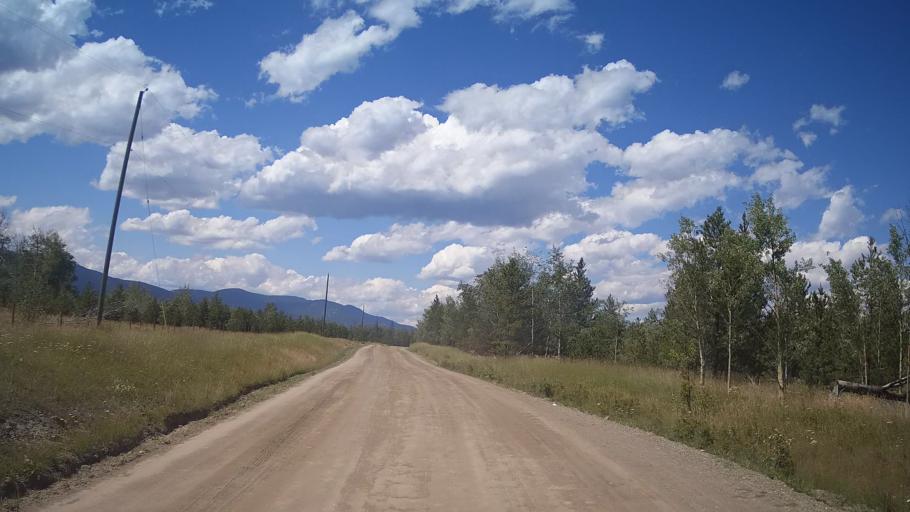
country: CA
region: British Columbia
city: Cache Creek
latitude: 51.2670
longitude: -121.7024
